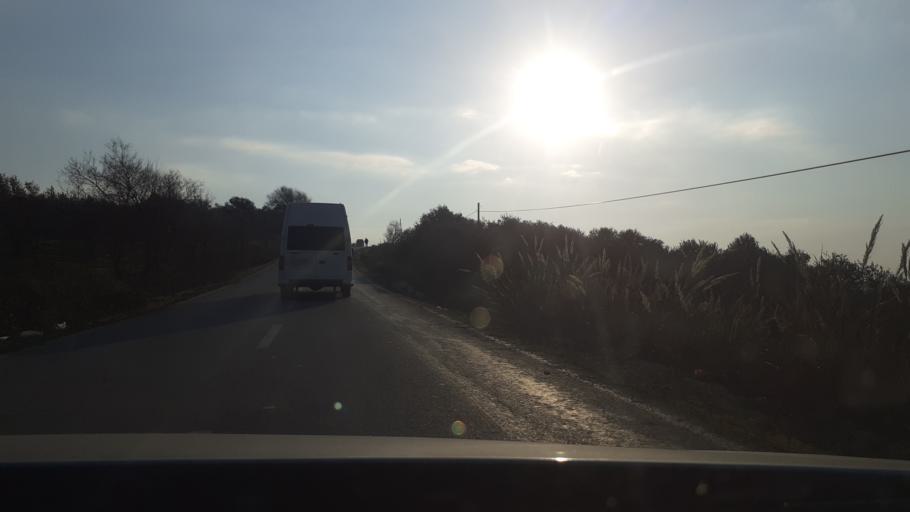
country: TR
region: Hatay
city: Oymakli
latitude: 36.1227
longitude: 36.3073
